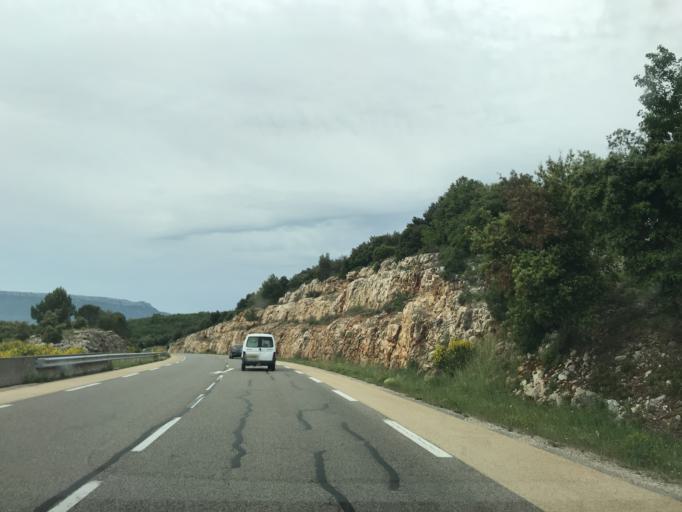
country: FR
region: Provence-Alpes-Cote d'Azur
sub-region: Departement du Var
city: Pourrieres
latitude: 43.5278
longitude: 5.8068
